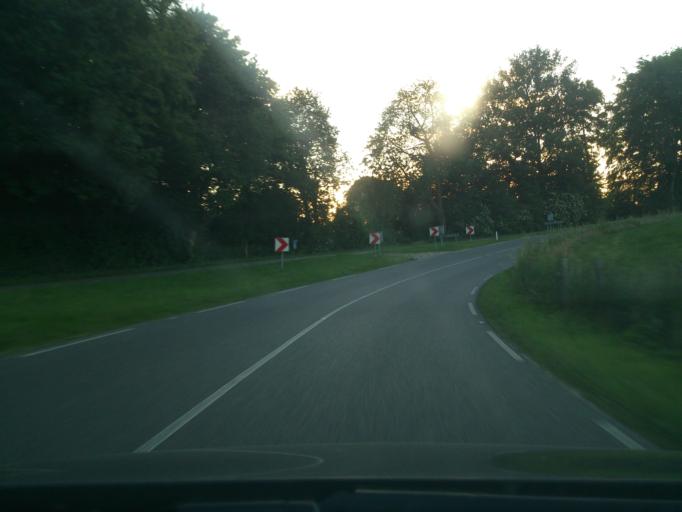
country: NL
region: Gelderland
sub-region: Gemeente Groesbeek
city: Groesbeek
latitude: 51.7932
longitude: 5.9308
